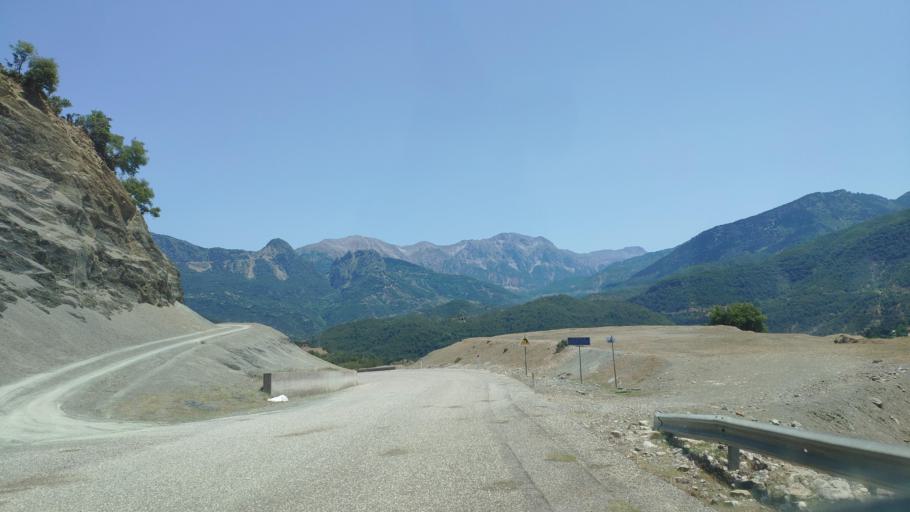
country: GR
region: Thessaly
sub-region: Nomos Kardhitsas
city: Anthiro
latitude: 39.1571
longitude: 21.3832
